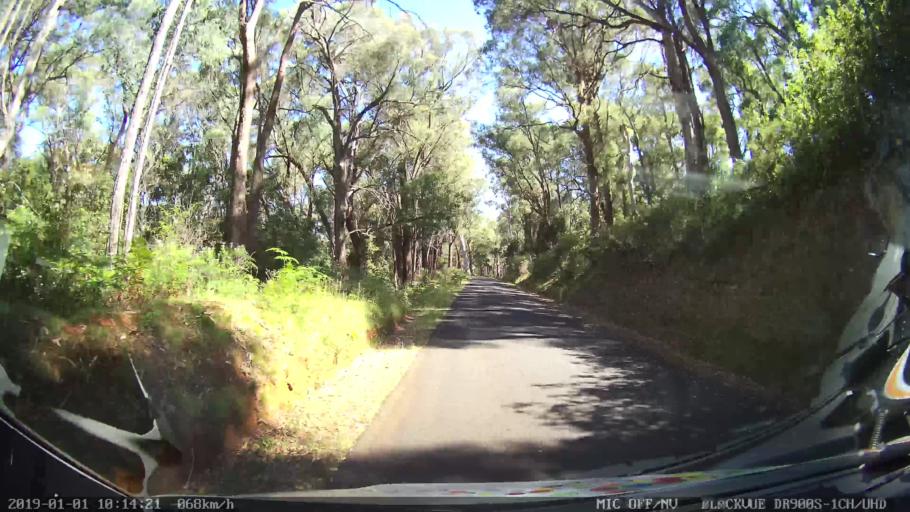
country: AU
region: New South Wales
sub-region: Snowy River
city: Jindabyne
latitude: -36.1131
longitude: 148.1608
